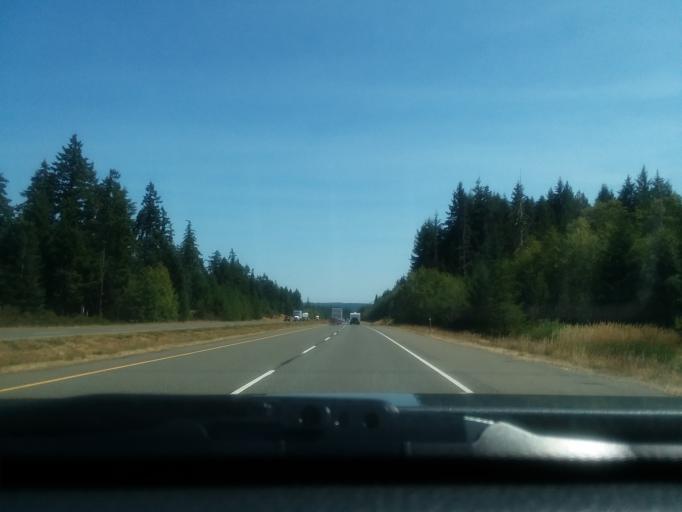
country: CA
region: British Columbia
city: Port Alberni
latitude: 49.4011
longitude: -124.6701
